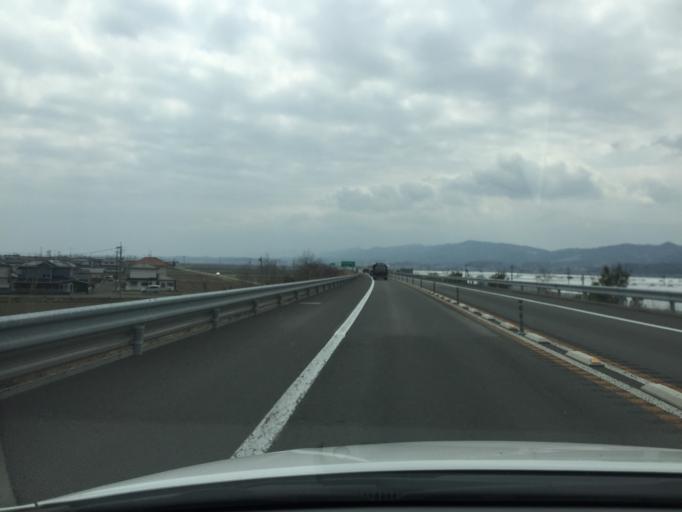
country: JP
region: Miyagi
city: Watari
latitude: 38.0090
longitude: 140.8821
